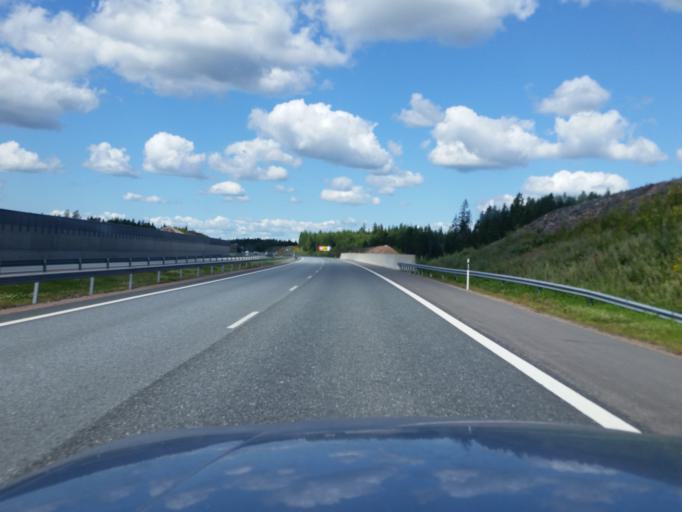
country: FI
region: Uusimaa
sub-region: Helsinki
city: Sammatti
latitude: 60.3651
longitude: 23.8775
